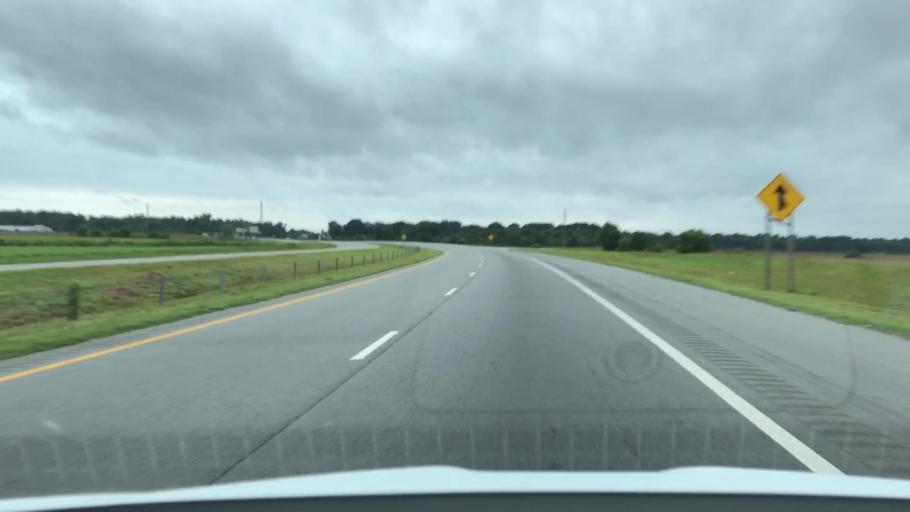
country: US
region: North Carolina
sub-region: Lenoir County
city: Kinston
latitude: 35.2657
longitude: -77.6794
